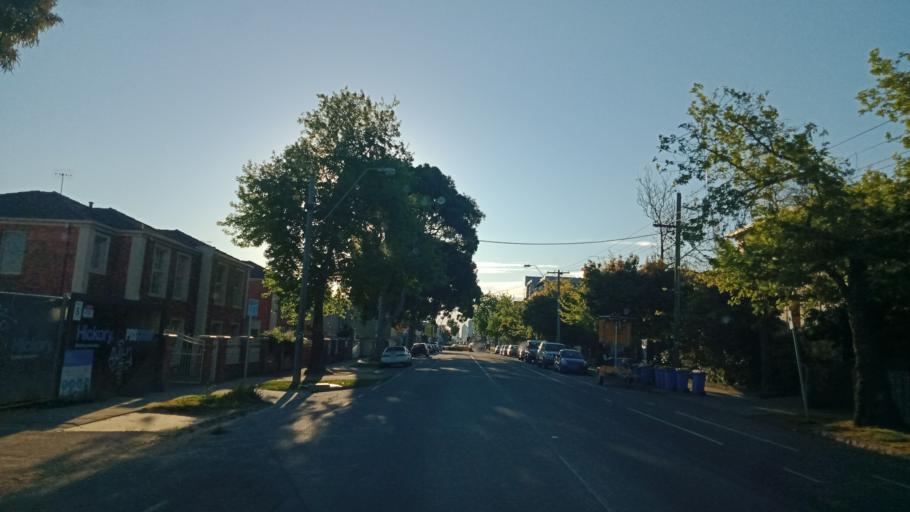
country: AU
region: Victoria
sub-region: Boroondara
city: Hawthorn East
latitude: -37.8244
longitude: 145.0505
